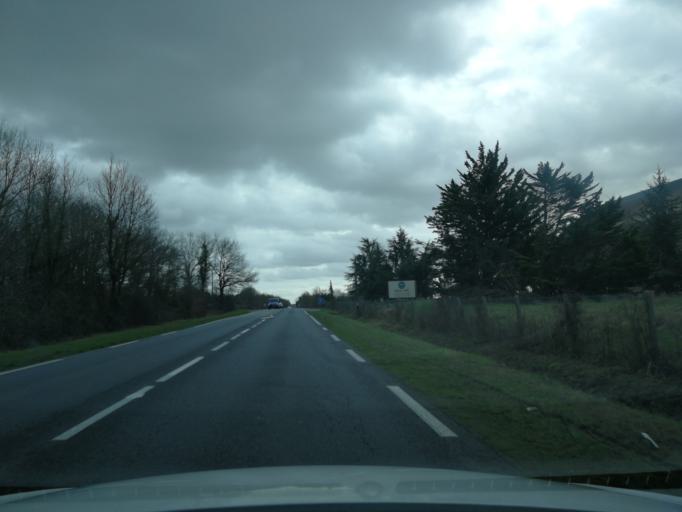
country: FR
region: Pays de la Loire
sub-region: Departement de la Loire-Atlantique
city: Geneston
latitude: 47.0827
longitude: -1.5258
